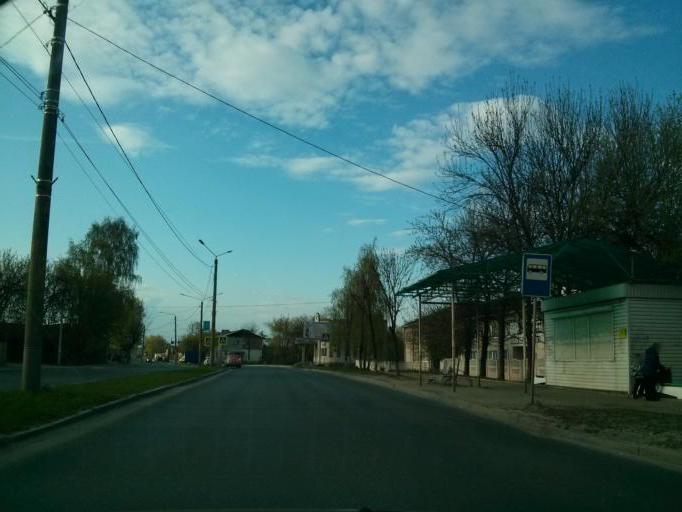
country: RU
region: Vladimir
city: Murom
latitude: 55.5831
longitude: 42.0367
